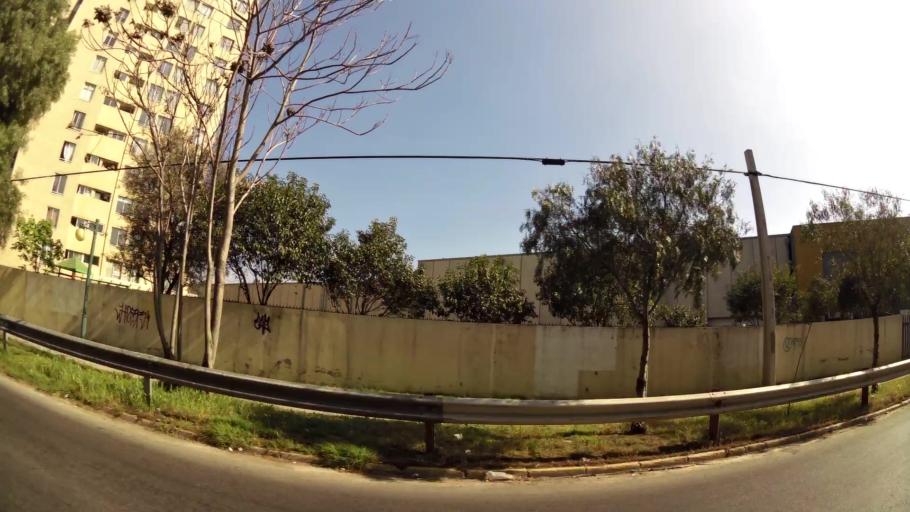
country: CL
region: Santiago Metropolitan
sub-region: Provincia de Santiago
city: Santiago
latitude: -33.4615
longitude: -70.6256
